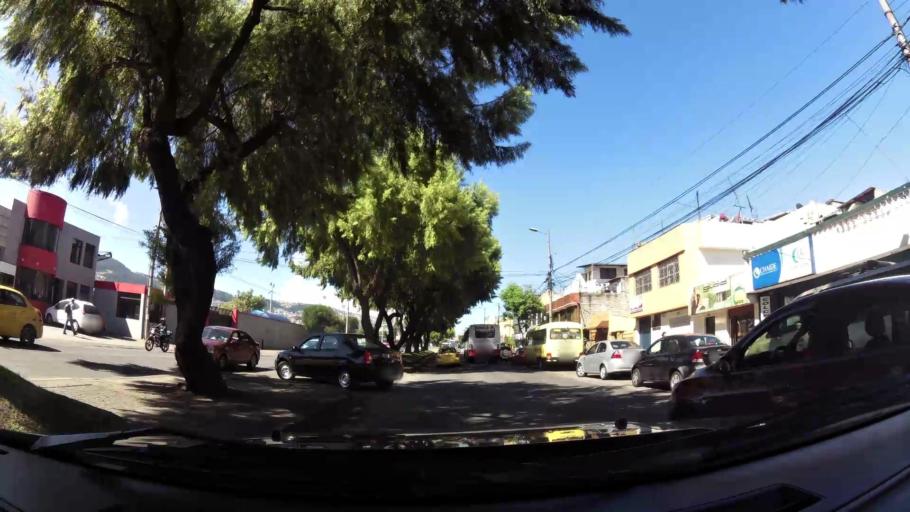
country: EC
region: Pichincha
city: Quito
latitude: -0.2510
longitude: -78.5310
